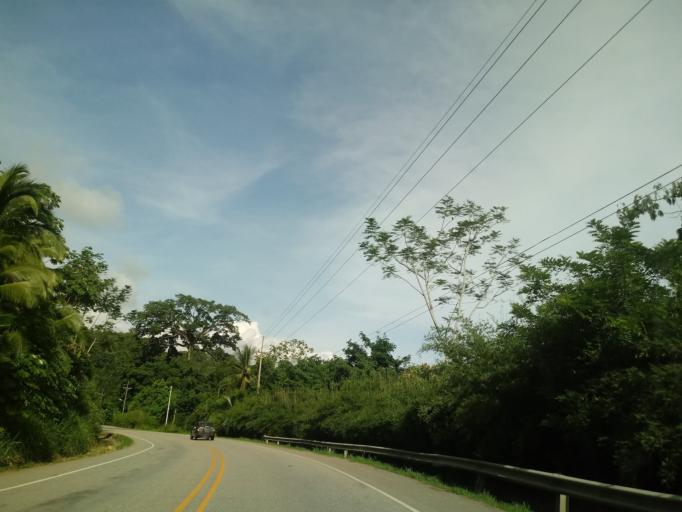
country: CR
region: San Jose
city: Daniel Flores
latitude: 9.2055
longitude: -83.7997
